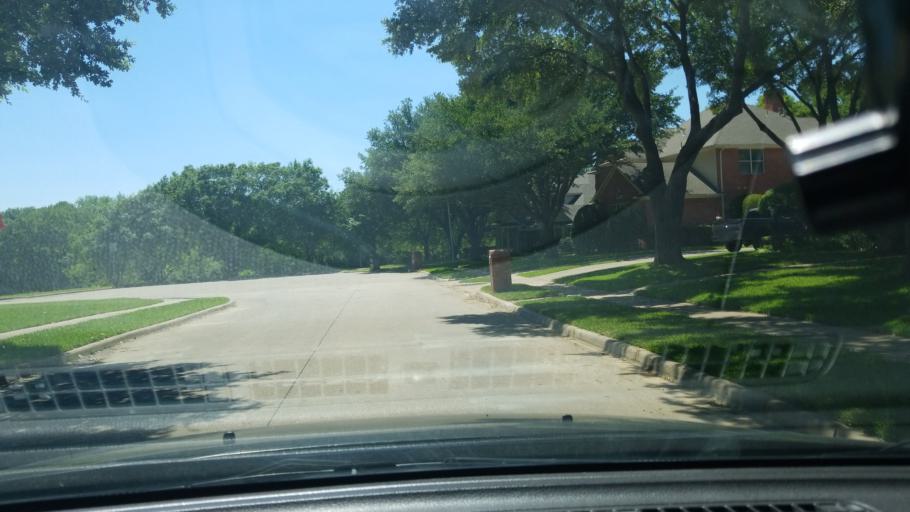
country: US
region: Texas
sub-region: Dallas County
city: Mesquite
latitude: 32.7599
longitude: -96.6102
